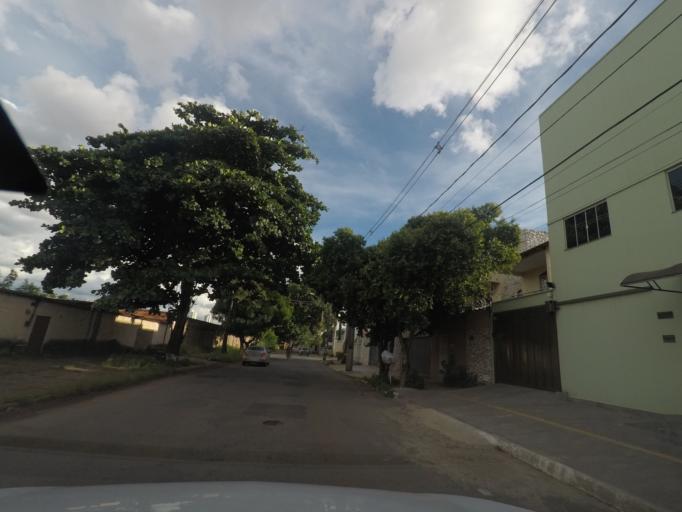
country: BR
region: Goias
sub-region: Goiania
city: Goiania
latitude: -16.6869
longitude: -49.2930
